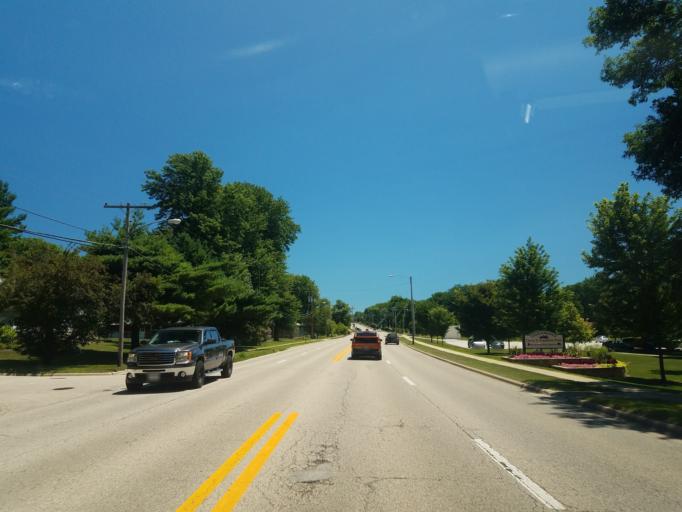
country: US
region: Illinois
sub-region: McLean County
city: Normal
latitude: 40.5105
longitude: -88.9768
